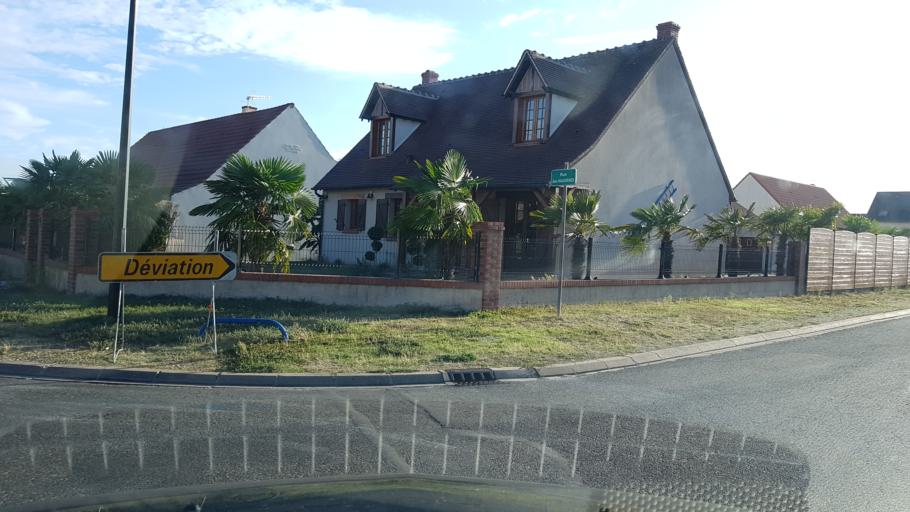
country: FR
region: Centre
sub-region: Departement du Loiret
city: Cerdon
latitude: 47.6884
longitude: 2.3358
